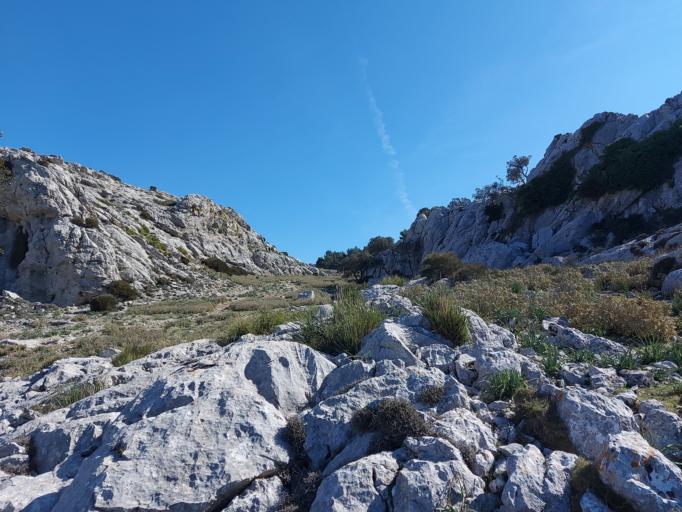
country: ES
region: Balearic Islands
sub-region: Illes Balears
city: Fornalutx
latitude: 39.7655
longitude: 2.7614
